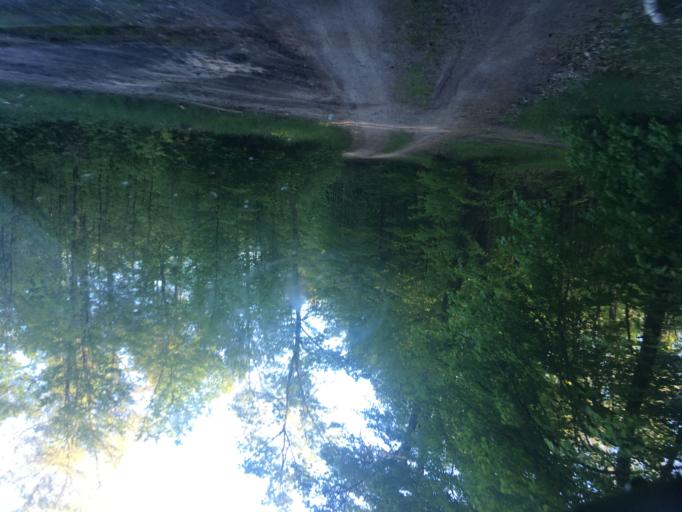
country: PL
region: Kujawsko-Pomorskie
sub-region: Powiat brodnicki
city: Gorzno
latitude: 53.2138
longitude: 19.7301
